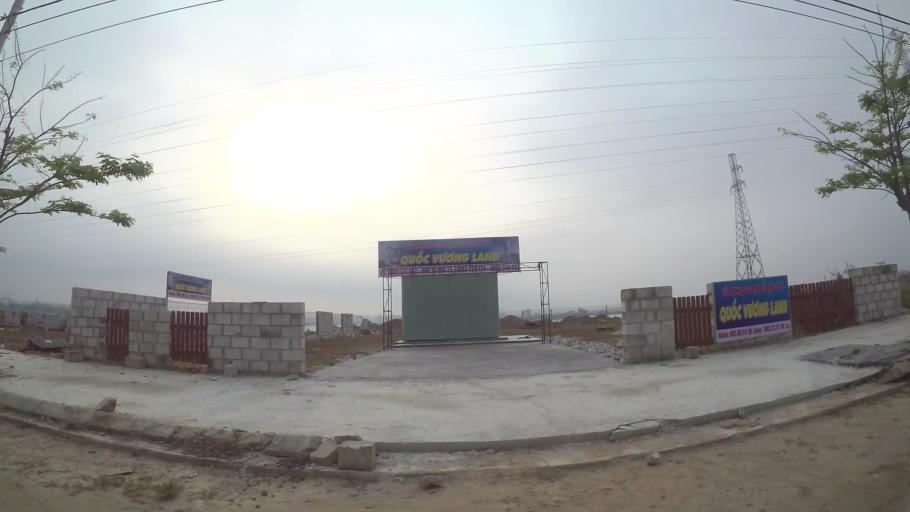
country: VN
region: Da Nang
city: Ngu Hanh Son
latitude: 16.0208
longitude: 108.2372
